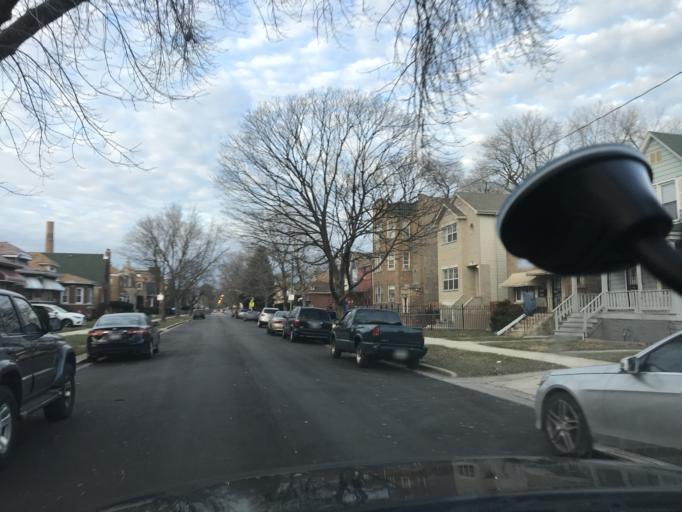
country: US
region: Indiana
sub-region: Lake County
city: Whiting
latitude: 41.7465
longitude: -87.5747
